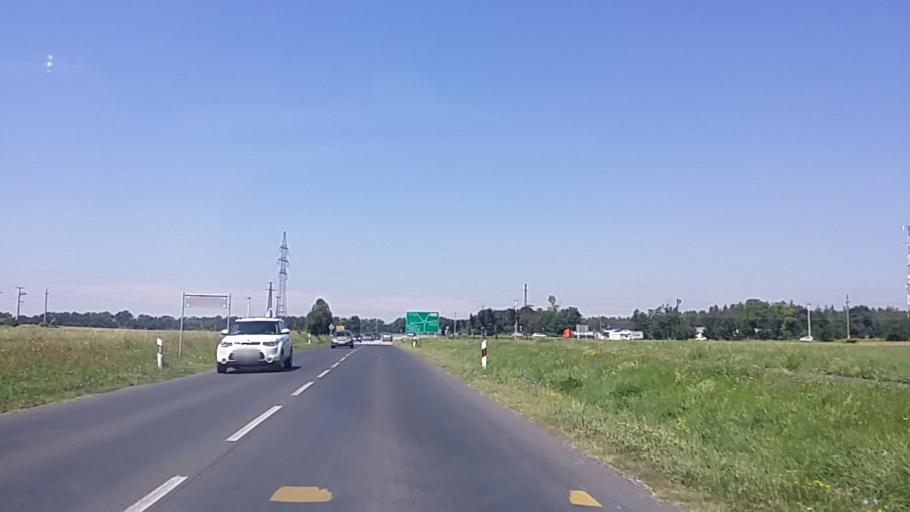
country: HU
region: Zala
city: Keszthely
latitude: 46.7763
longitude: 17.2299
